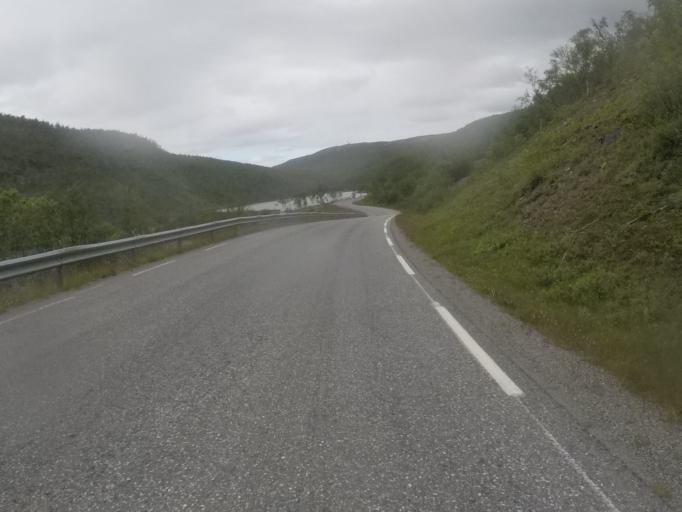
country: NO
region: Finnmark Fylke
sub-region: Alta
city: Alta
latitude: 69.7390
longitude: 23.3878
